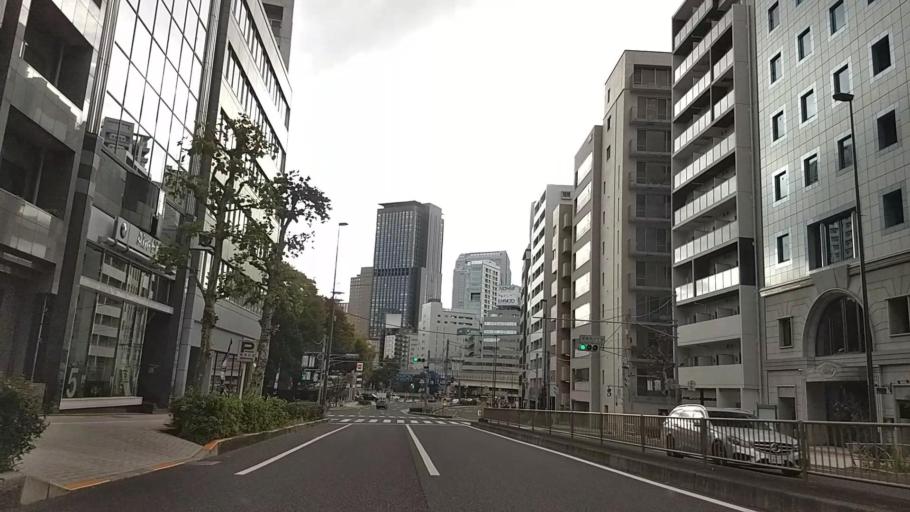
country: JP
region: Tokyo
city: Tokyo
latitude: 35.6567
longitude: 139.7445
